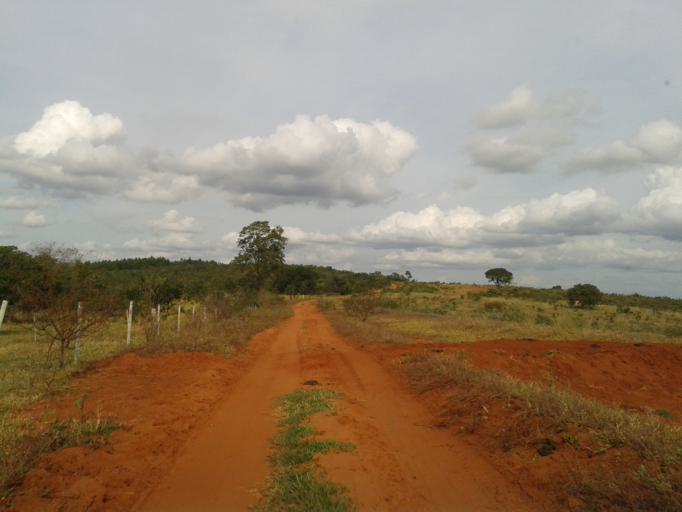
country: BR
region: Minas Gerais
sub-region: Campina Verde
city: Campina Verde
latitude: -19.4488
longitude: -49.6099
